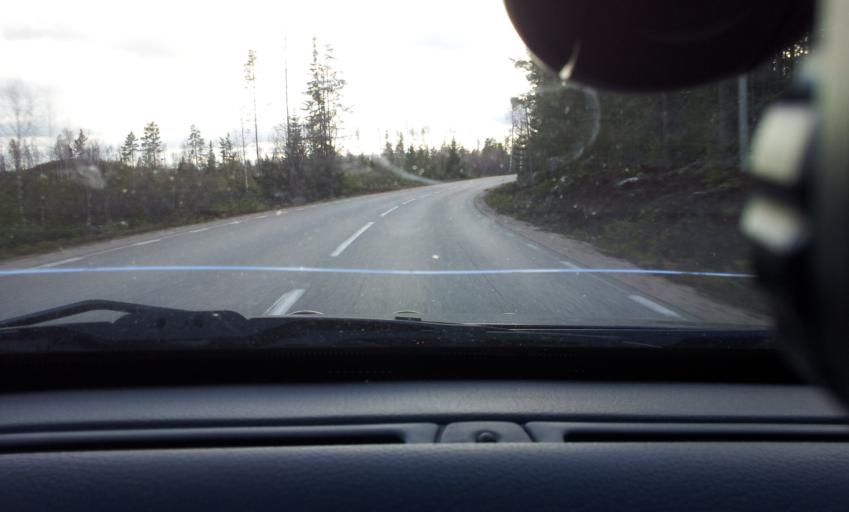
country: SE
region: Jaemtland
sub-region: Harjedalens Kommun
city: Sveg
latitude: 62.1239
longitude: 15.0174
